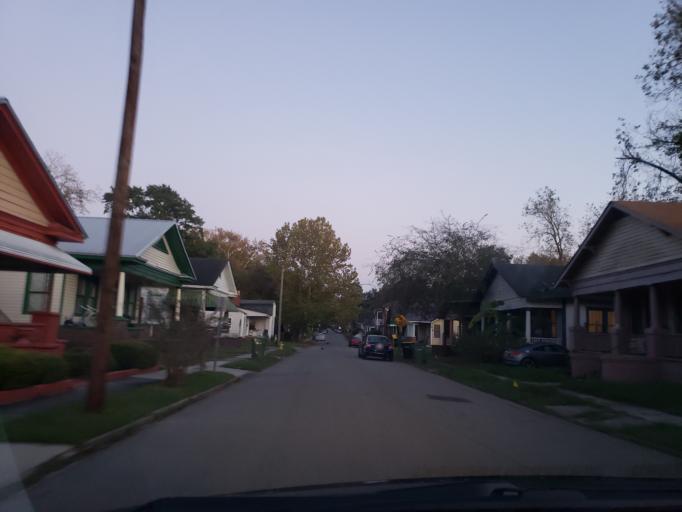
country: US
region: Georgia
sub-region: Chatham County
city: Savannah
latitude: 32.0513
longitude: -81.0829
